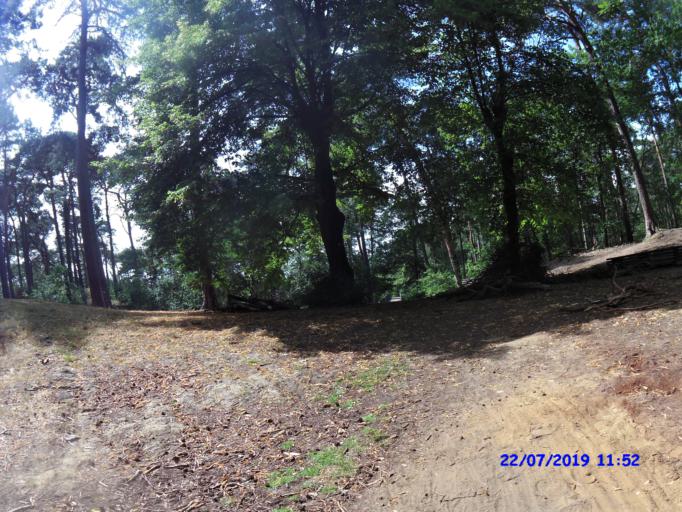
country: BE
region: Flanders
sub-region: Provincie Antwerpen
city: Westerlo
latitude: 51.0854
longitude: 4.8960
